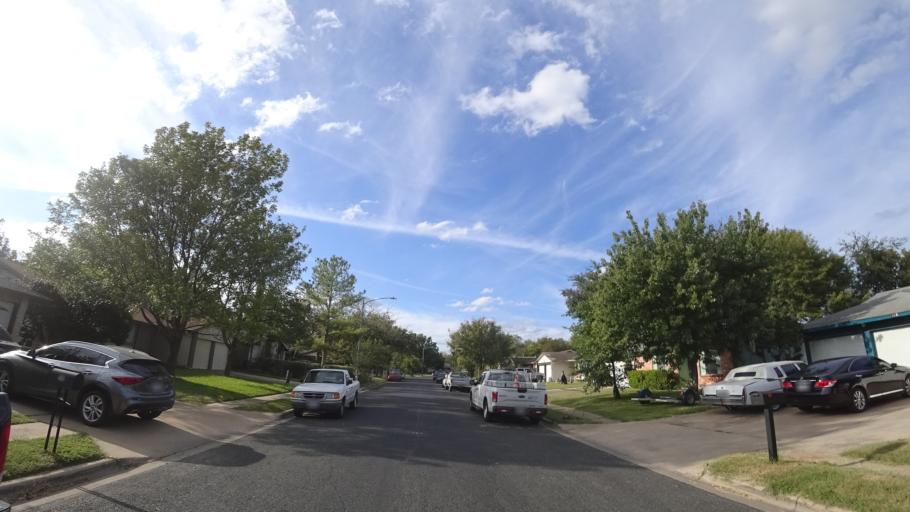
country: US
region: Texas
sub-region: Travis County
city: Onion Creek
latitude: 30.1910
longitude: -97.7558
